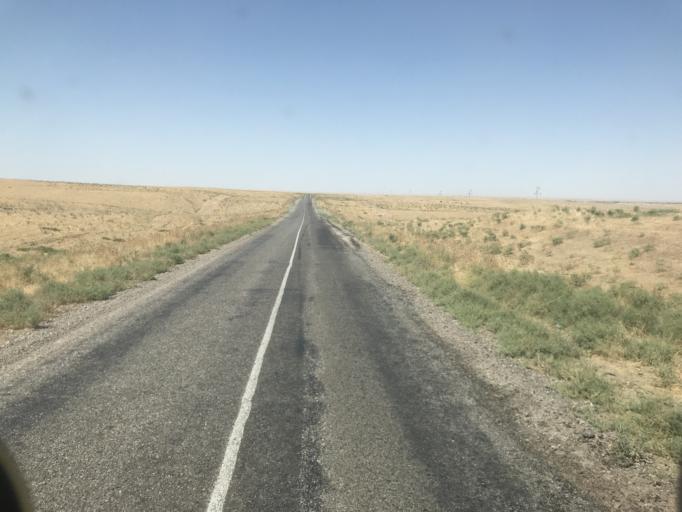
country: UZ
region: Toshkent
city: Chinoz
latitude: 41.1591
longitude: 68.6619
